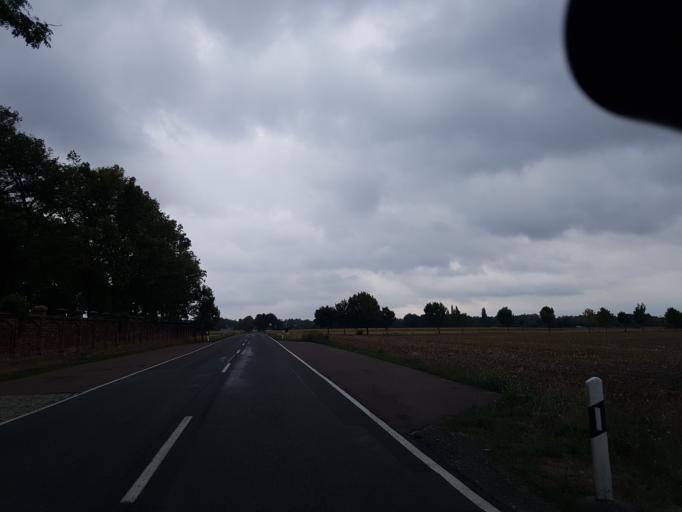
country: DE
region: Saxony-Anhalt
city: Loburg
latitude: 52.1259
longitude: 12.0900
